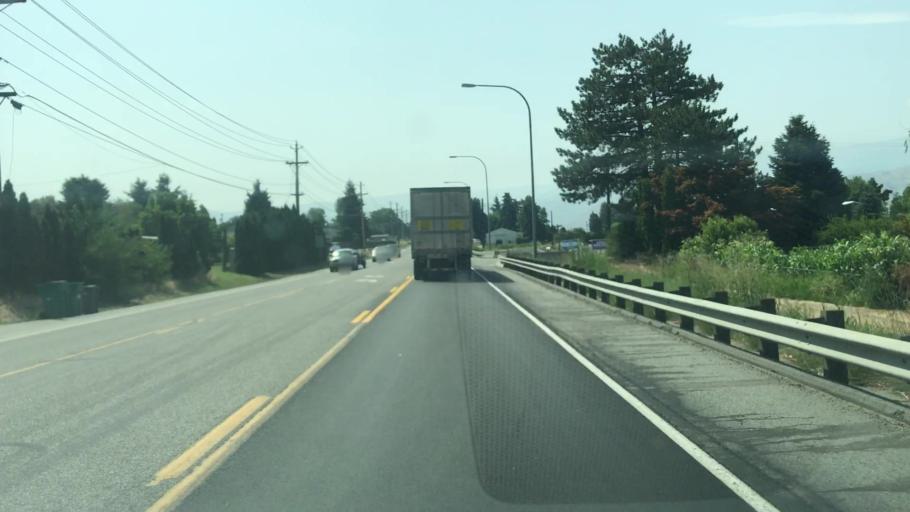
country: US
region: Washington
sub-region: Douglas County
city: East Wenatchee Bench
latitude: 47.4614
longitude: -120.2975
